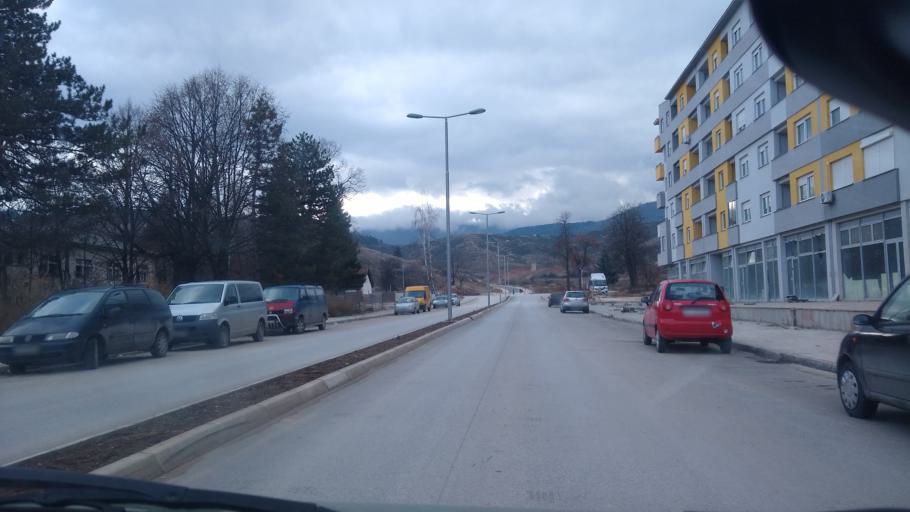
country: MK
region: Bitola
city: Bitola
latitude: 41.0223
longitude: 21.3285
